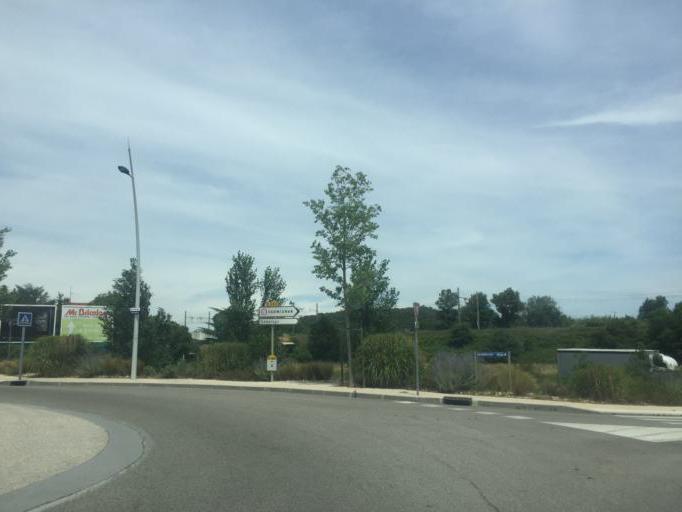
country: FR
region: Languedoc-Roussillon
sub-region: Departement du Gard
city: Bagnols-sur-Ceze
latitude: 44.1721
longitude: 4.6202
